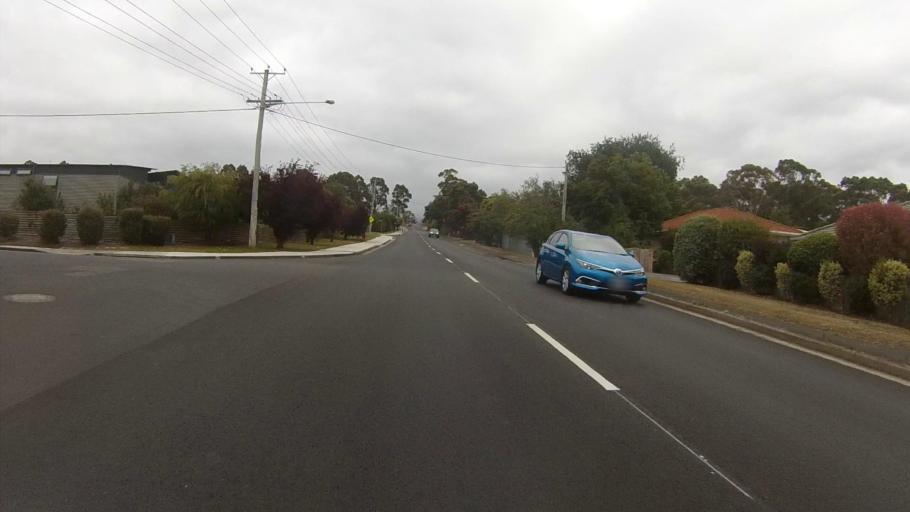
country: AU
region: Tasmania
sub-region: Kingborough
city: Kingston
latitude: -42.9712
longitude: 147.2927
